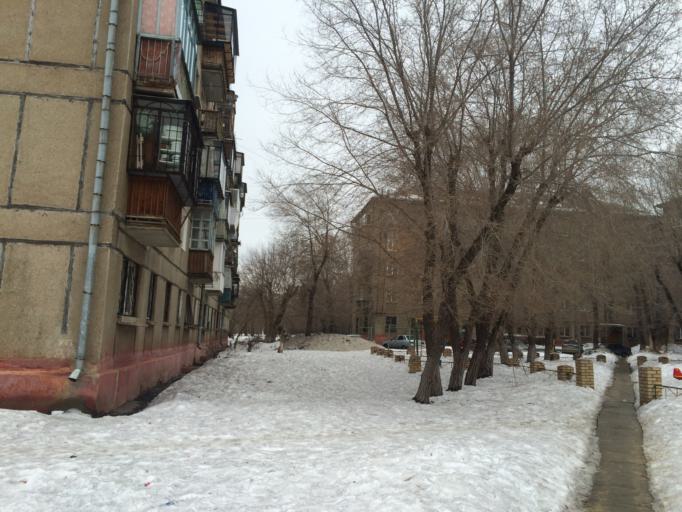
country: RU
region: Chelyabinsk
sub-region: Gorod Magnitogorsk
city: Magnitogorsk
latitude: 53.4098
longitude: 58.9668
